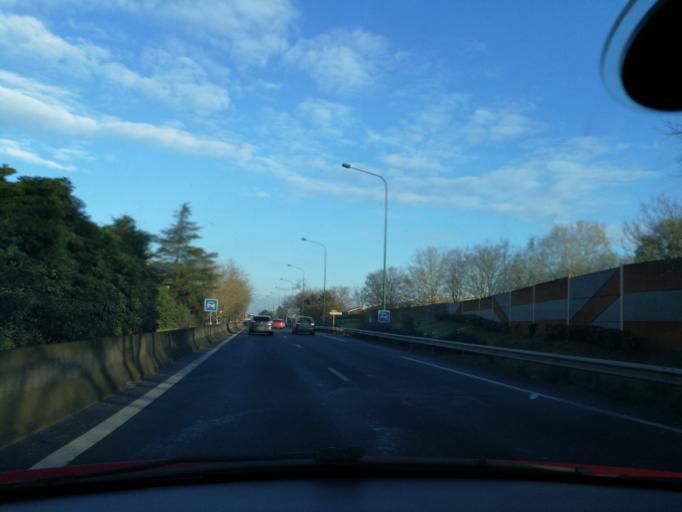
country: FR
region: Midi-Pyrenees
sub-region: Departement de la Haute-Garonne
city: Blagnac
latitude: 43.6320
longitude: 1.3813
